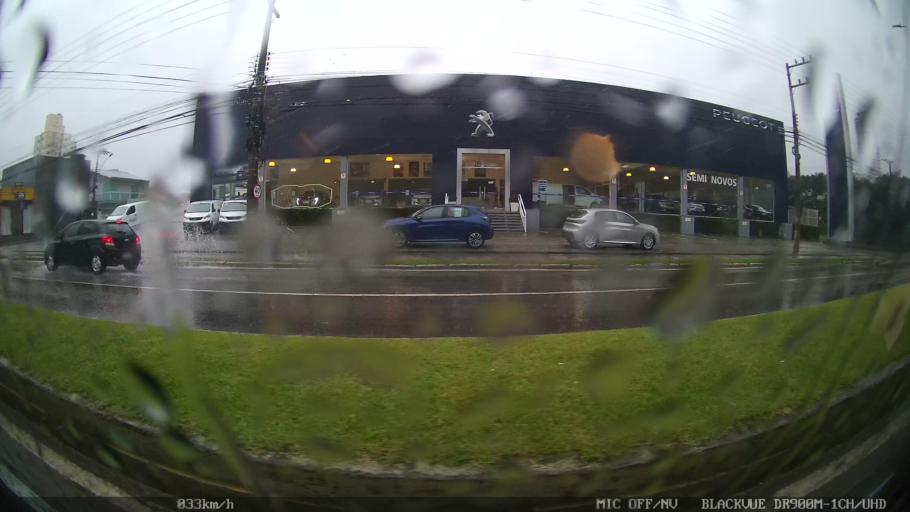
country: BR
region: Santa Catarina
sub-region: Balneario Camboriu
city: Balneario Camboriu
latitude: -26.9514
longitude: -48.6405
